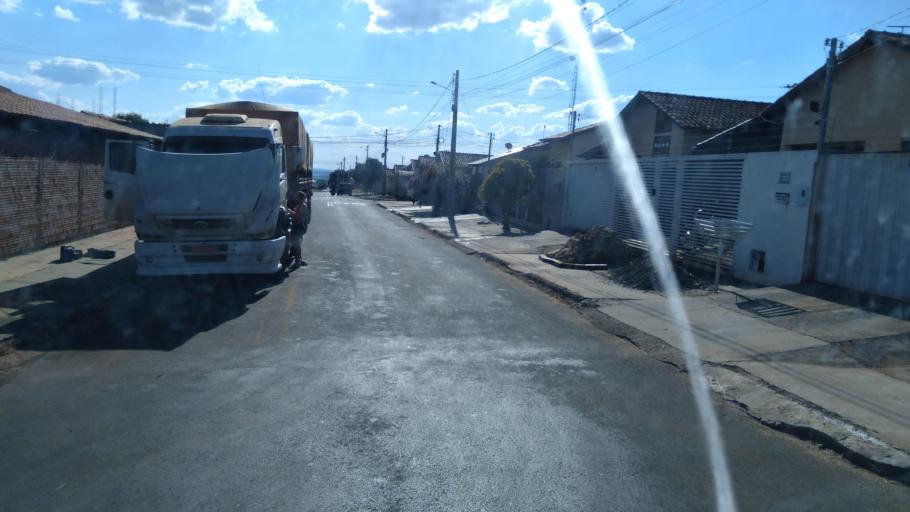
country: BR
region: Goias
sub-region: Mineiros
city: Mineiros
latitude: -17.5458
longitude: -52.5383
